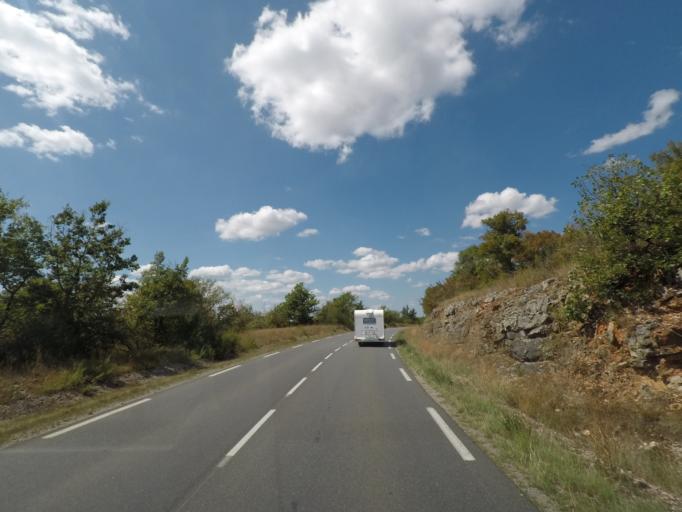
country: FR
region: Midi-Pyrenees
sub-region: Departement du Lot
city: Lacapelle-Marival
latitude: 44.6251
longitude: 1.8925
